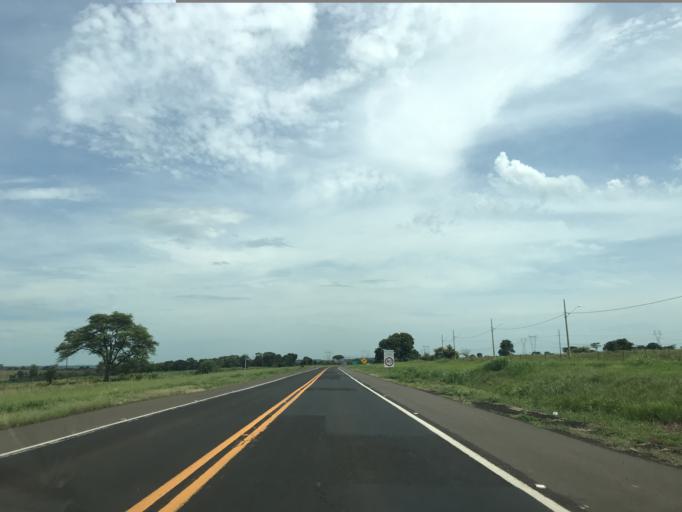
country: BR
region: Sao Paulo
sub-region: Nova Granada
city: Nova Granada
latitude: -20.3473
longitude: -49.2151
